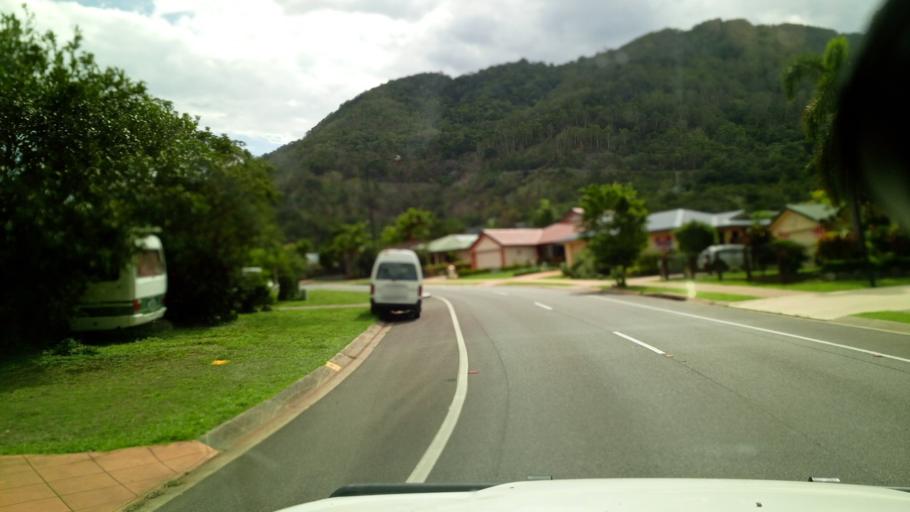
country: AU
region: Queensland
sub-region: Cairns
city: Woree
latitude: -16.9245
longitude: 145.7278
